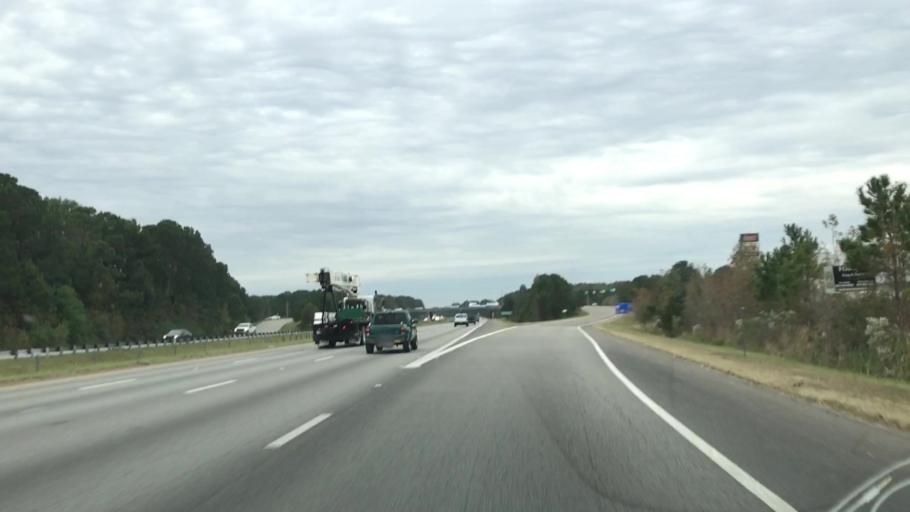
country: US
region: South Carolina
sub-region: Berkeley County
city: Ladson
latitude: 32.9958
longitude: -80.0907
